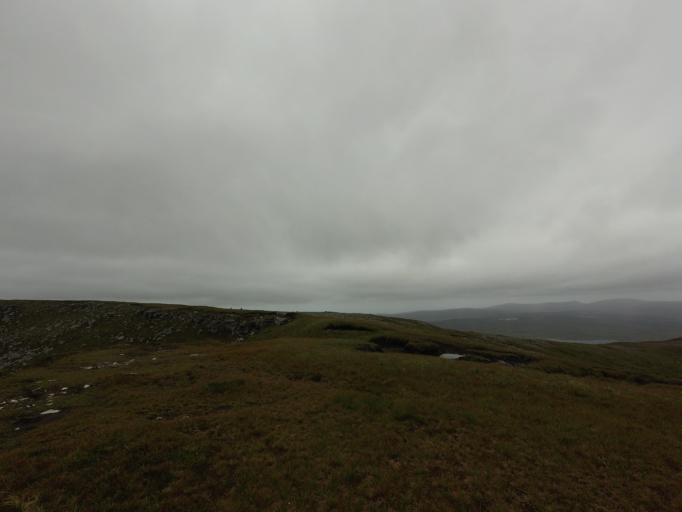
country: IE
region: Ulster
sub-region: County Donegal
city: Killybegs
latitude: 54.6477
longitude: -8.6913
